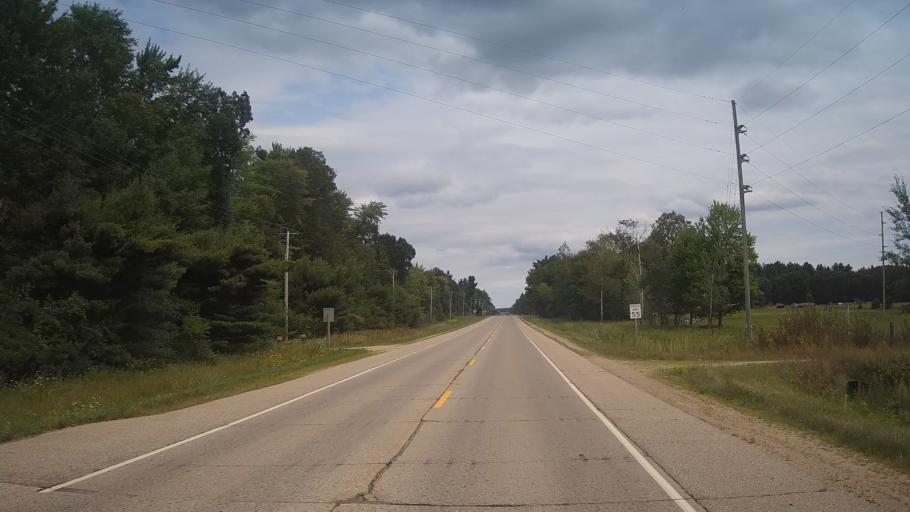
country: US
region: Wisconsin
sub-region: Waushara County
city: Redgranite
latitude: 44.0375
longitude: -89.0867
